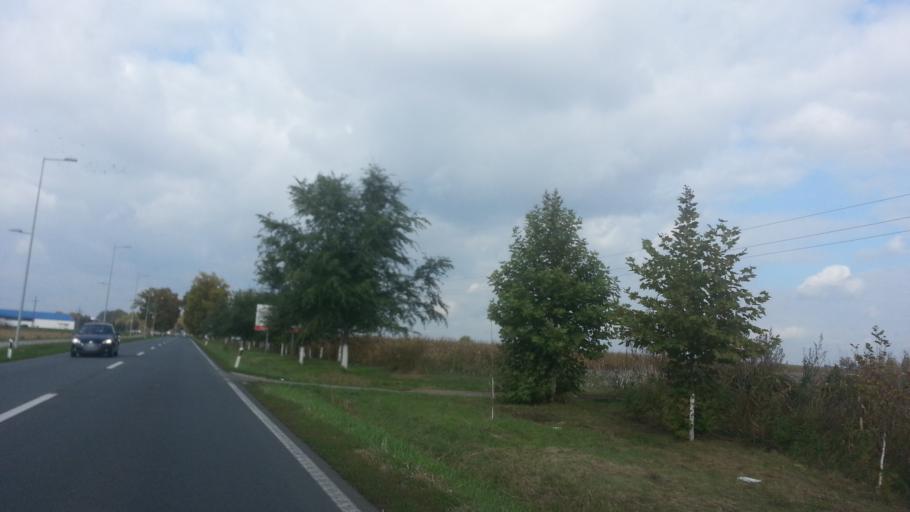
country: RS
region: Autonomna Pokrajina Vojvodina
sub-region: Sremski Okrug
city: Stara Pazova
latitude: 44.9653
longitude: 20.1864
